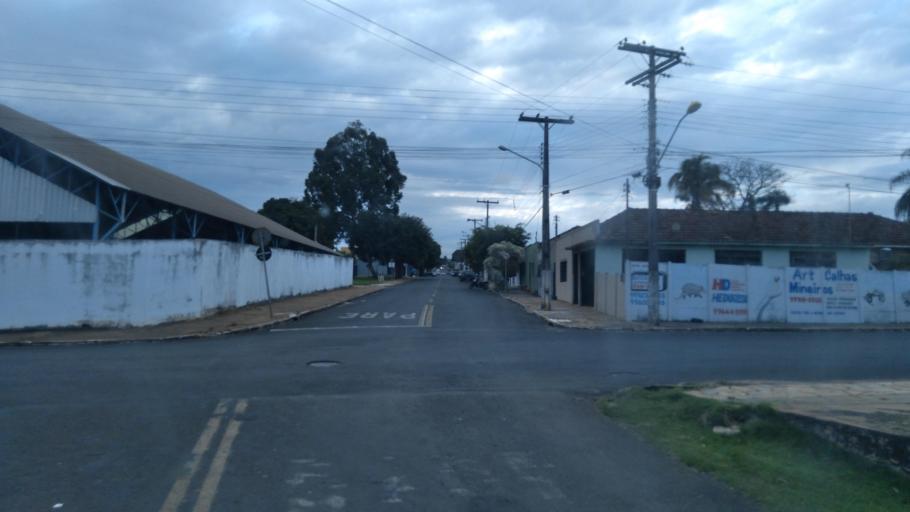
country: BR
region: Goias
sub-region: Mineiros
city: Mineiros
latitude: -17.5689
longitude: -52.5485
